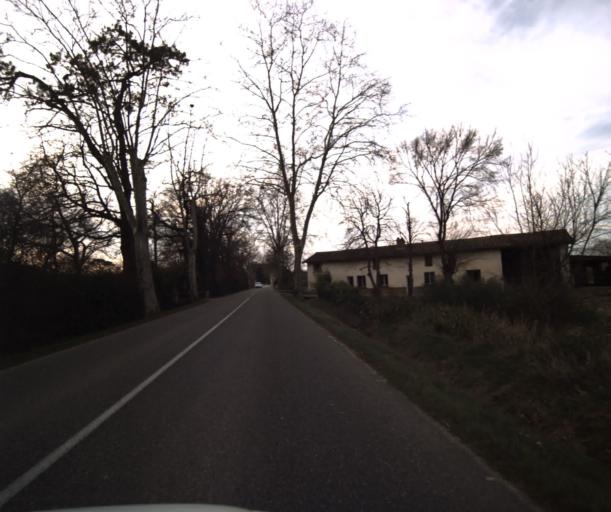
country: FR
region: Midi-Pyrenees
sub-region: Departement du Tarn-et-Garonne
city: Campsas
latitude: 43.8991
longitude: 1.3124
